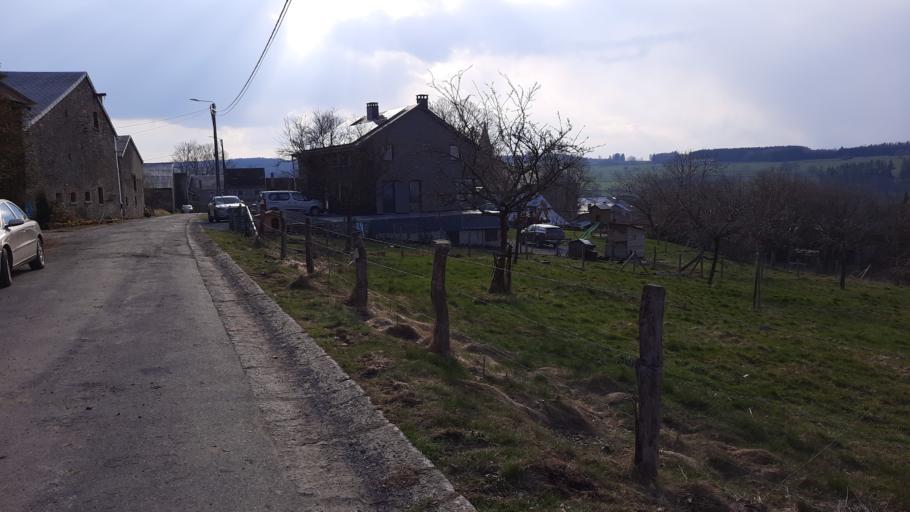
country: BE
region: Wallonia
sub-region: Province du Luxembourg
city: Manhay
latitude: 50.2813
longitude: 5.7182
